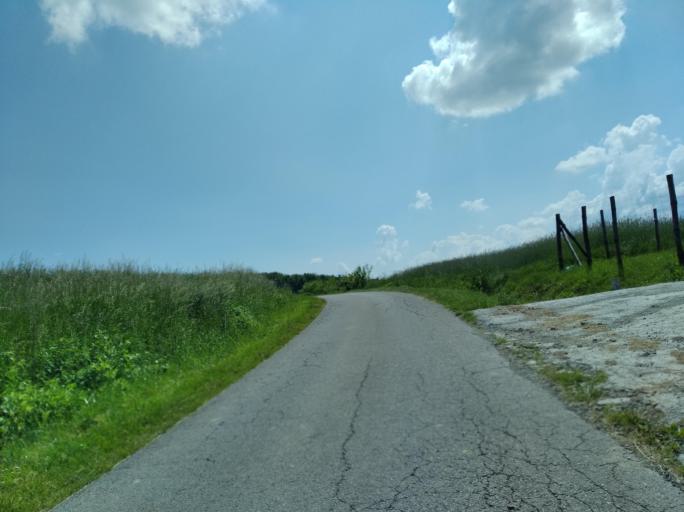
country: PL
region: Subcarpathian Voivodeship
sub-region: Powiat ropczycko-sedziszowski
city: Wielopole Skrzynskie
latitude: 49.9844
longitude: 21.6076
